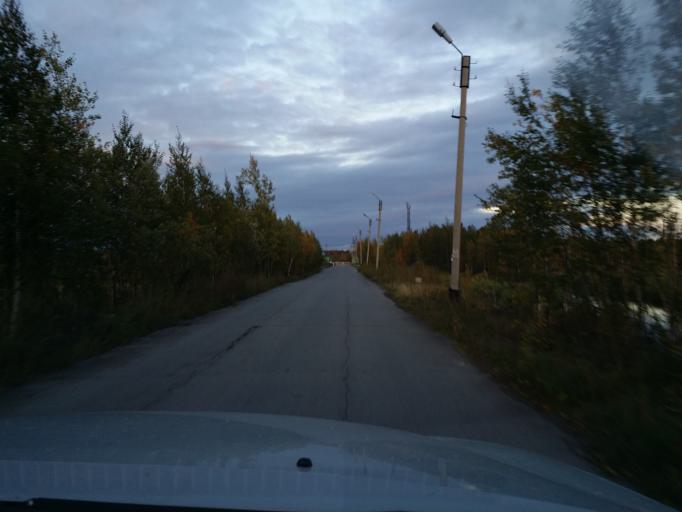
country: RU
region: Khanty-Mansiyskiy Avtonomnyy Okrug
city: Megion
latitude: 61.0833
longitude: 76.1621
